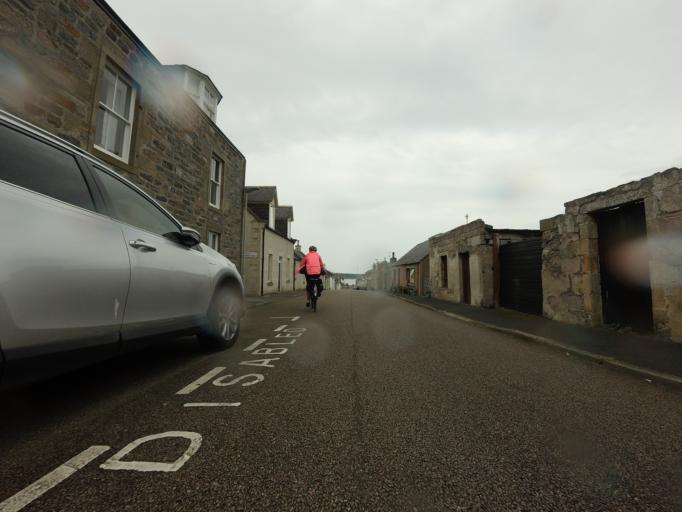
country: GB
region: Scotland
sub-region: Moray
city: Cullen
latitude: 57.6892
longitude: -2.8199
